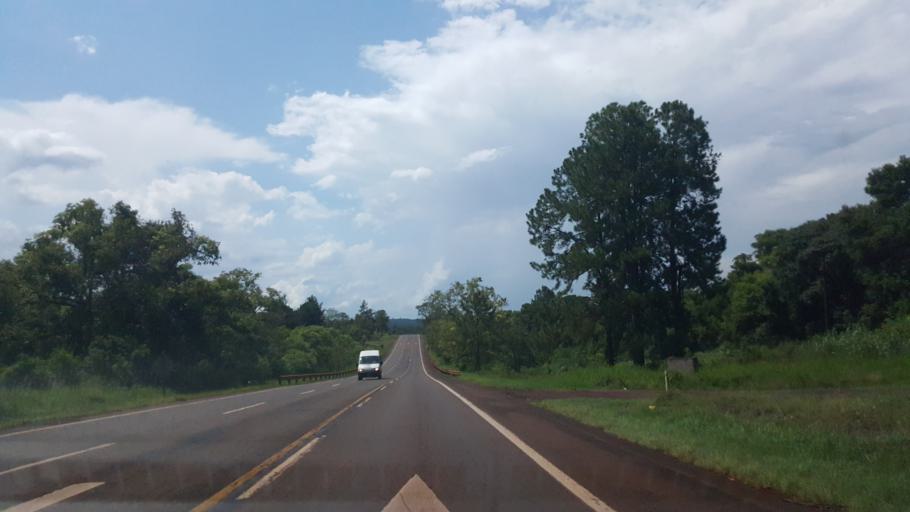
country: AR
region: Misiones
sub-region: Departamento de Eldorado
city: Eldorado
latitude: -26.3691
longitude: -54.6234
